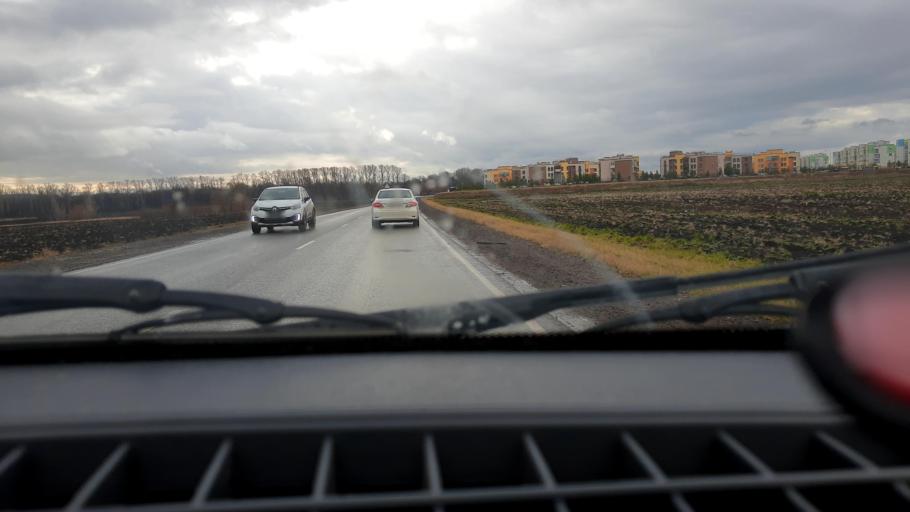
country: RU
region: Bashkortostan
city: Ufa
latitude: 54.8016
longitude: 55.9631
